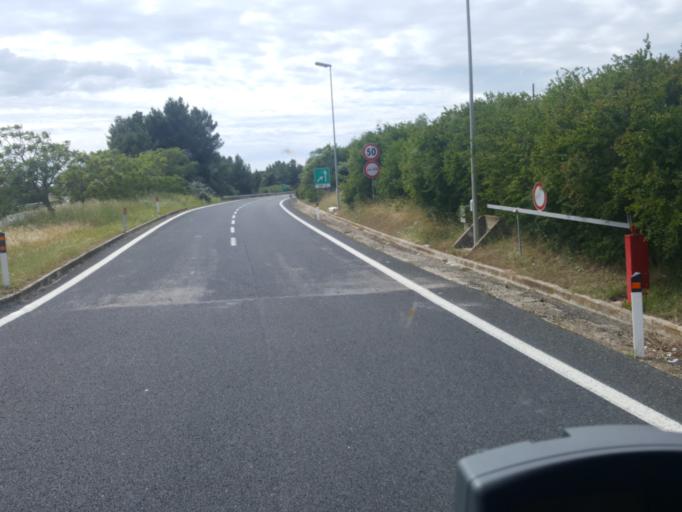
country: IT
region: Latium
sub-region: Citta metropolitana di Roma Capitale
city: Ara Nova
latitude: 41.9167
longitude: 12.2092
